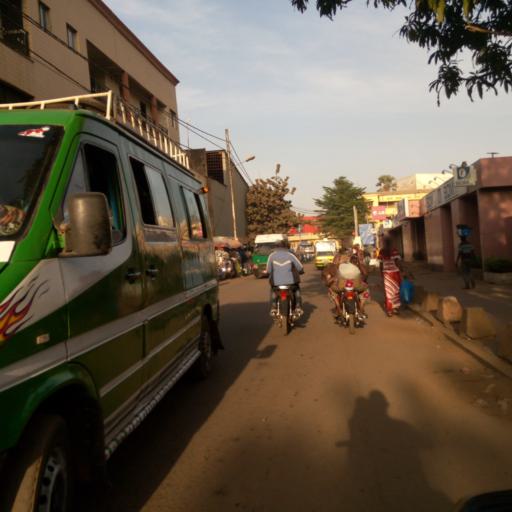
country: ML
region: Bamako
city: Bamako
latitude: 12.6436
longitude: -8.0012
